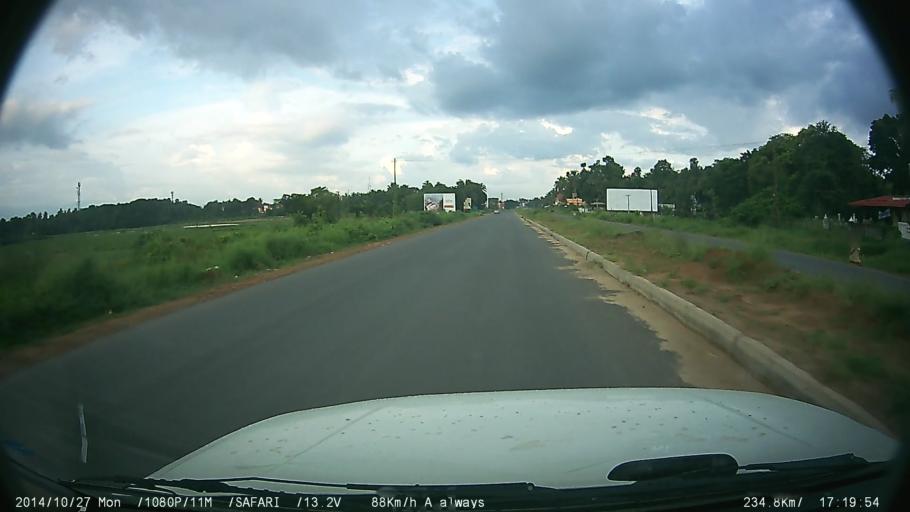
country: IN
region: Kerala
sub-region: Palakkad district
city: Palakkad
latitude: 10.6426
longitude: 76.5327
